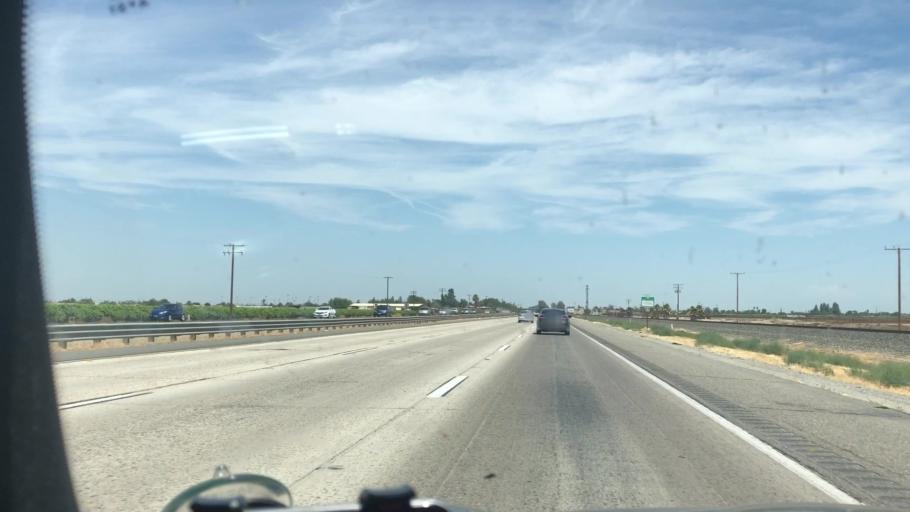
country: US
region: California
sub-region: Kern County
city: McFarland
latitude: 35.6608
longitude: -119.2229
